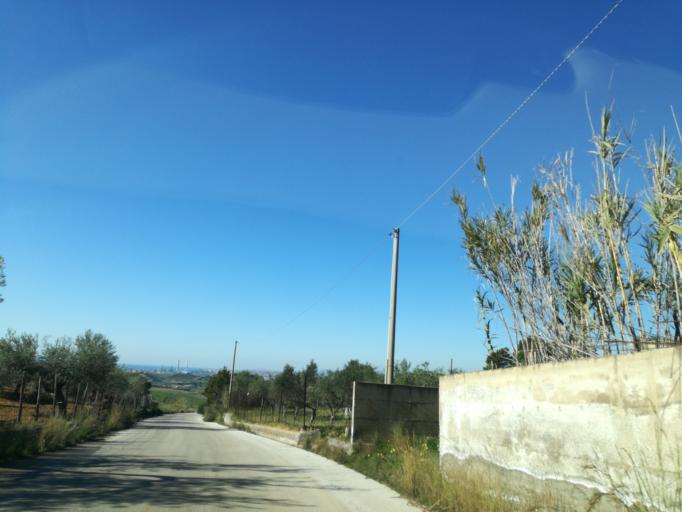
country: IT
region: Sicily
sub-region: Provincia di Caltanissetta
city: Niscemi
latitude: 37.0606
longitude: 14.3513
